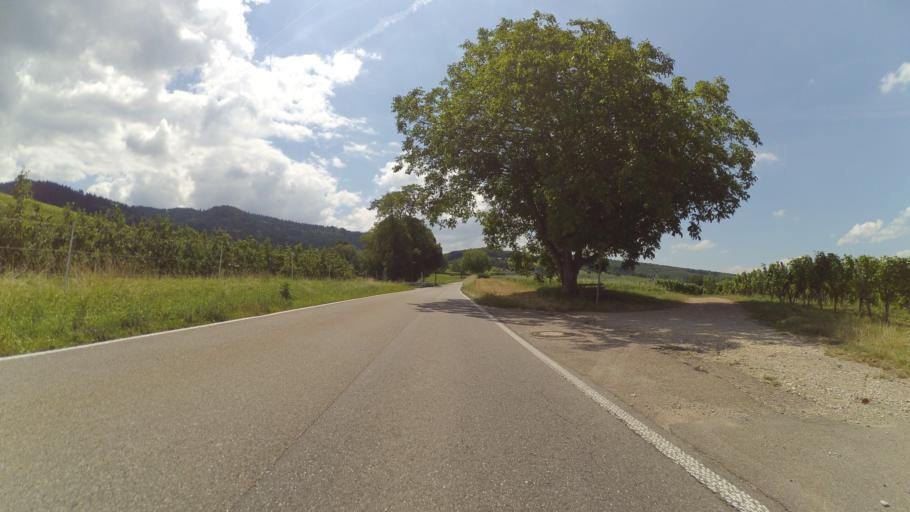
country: DE
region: Baden-Wuerttemberg
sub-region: Freiburg Region
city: Sulzburg
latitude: 47.8325
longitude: 7.6826
